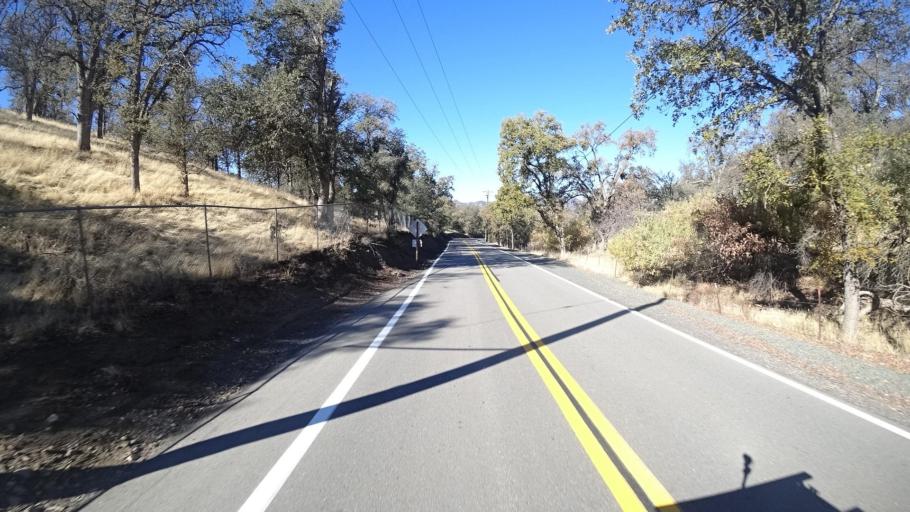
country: US
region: California
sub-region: Kern County
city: Alta Sierra
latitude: 35.7212
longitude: -118.6932
